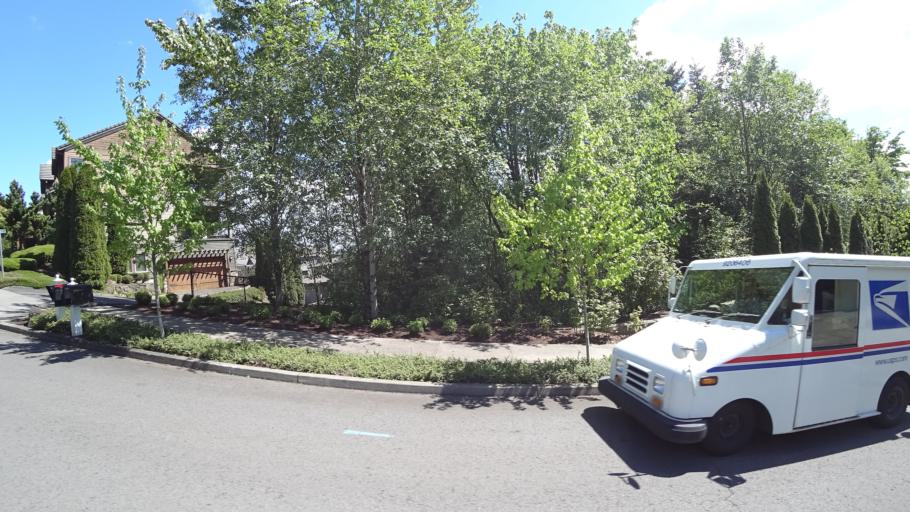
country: US
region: Oregon
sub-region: Washington County
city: West Haven
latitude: 45.5518
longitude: -122.7774
